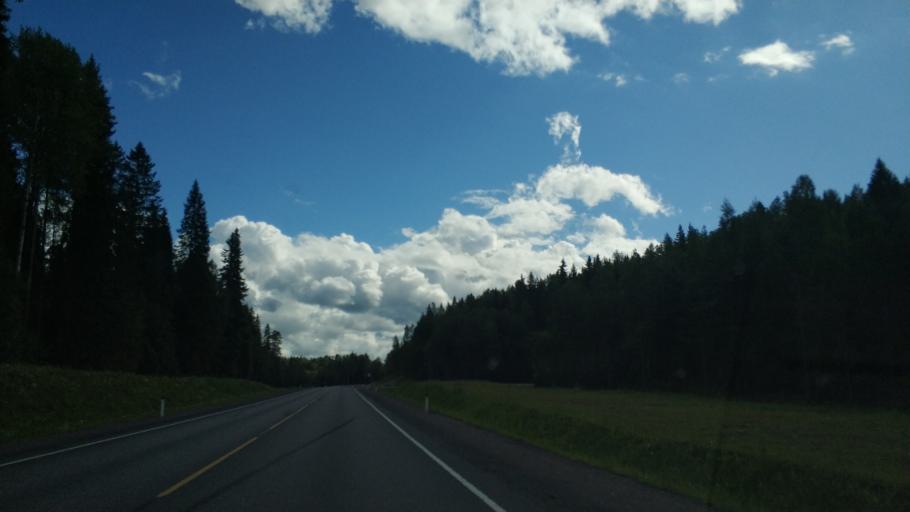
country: RU
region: Republic of Karelia
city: Ruskeala
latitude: 61.9091
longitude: 30.6294
